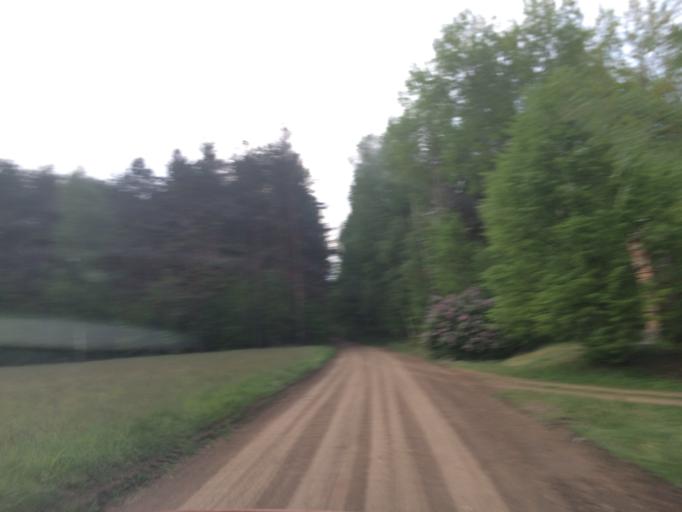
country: PL
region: Warmian-Masurian Voivodeship
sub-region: Powiat nowomiejski
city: Kurzetnik
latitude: 53.3552
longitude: 19.5174
